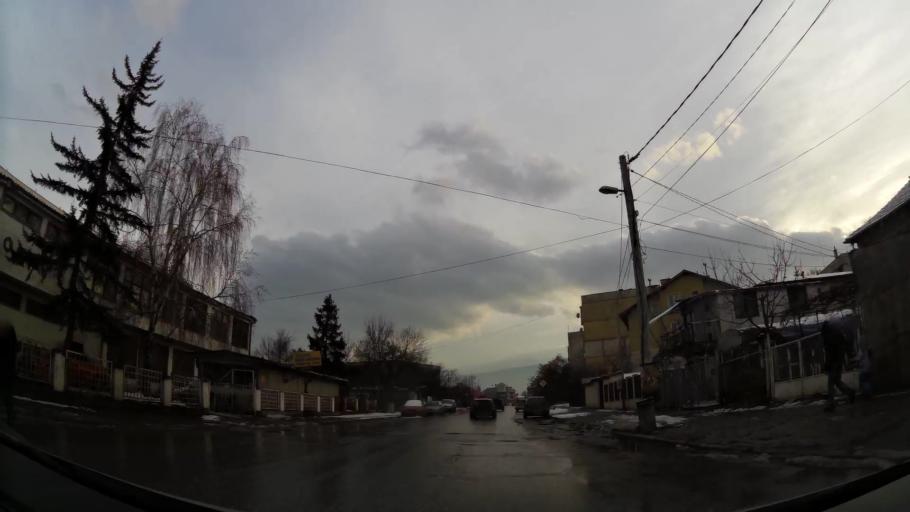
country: BG
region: Sofia-Capital
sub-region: Stolichna Obshtina
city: Sofia
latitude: 42.7199
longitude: 23.3436
